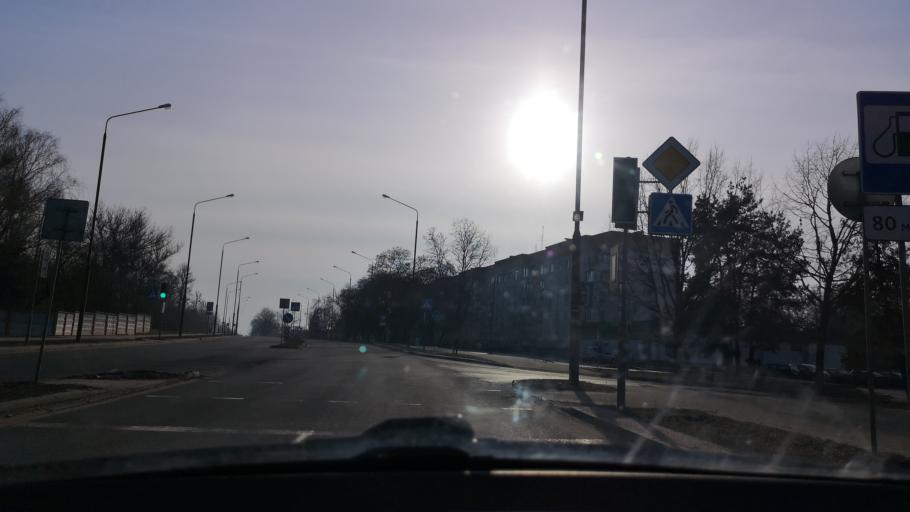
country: BY
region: Brest
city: Brest
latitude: 52.1385
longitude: 23.6765
